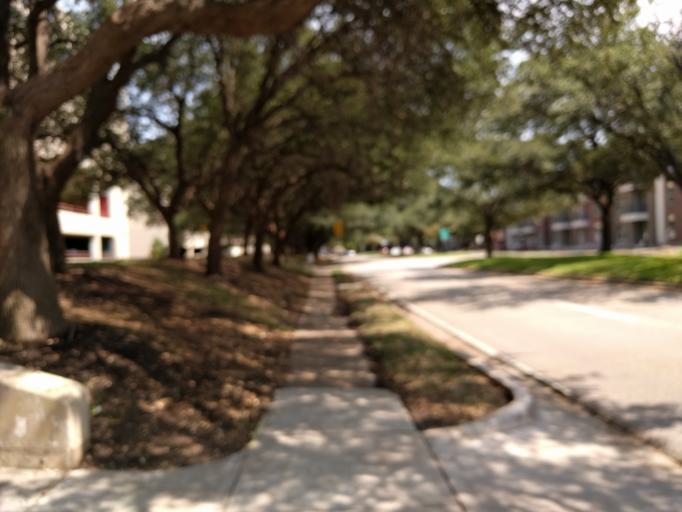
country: US
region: Texas
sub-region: Dallas County
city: Richardson
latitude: 32.9214
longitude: -96.7712
